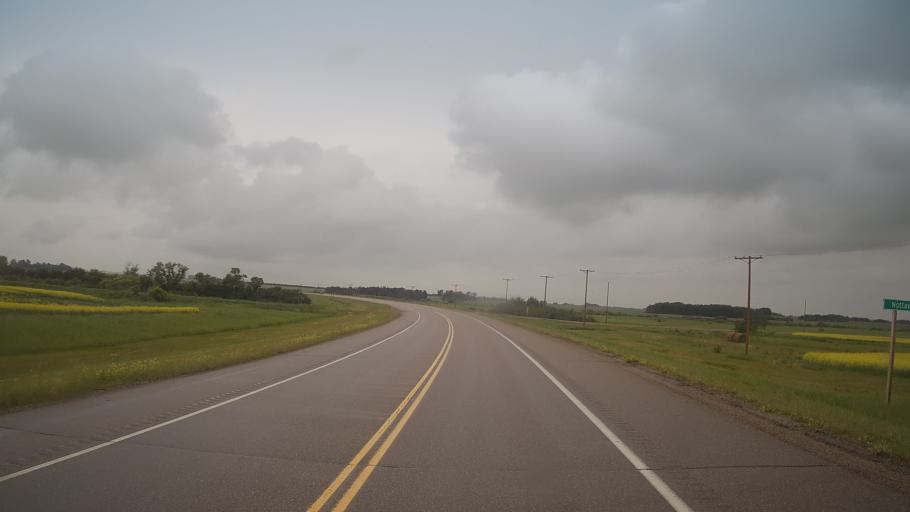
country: CA
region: Saskatchewan
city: Wilkie
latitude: 52.4336
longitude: -108.9273
